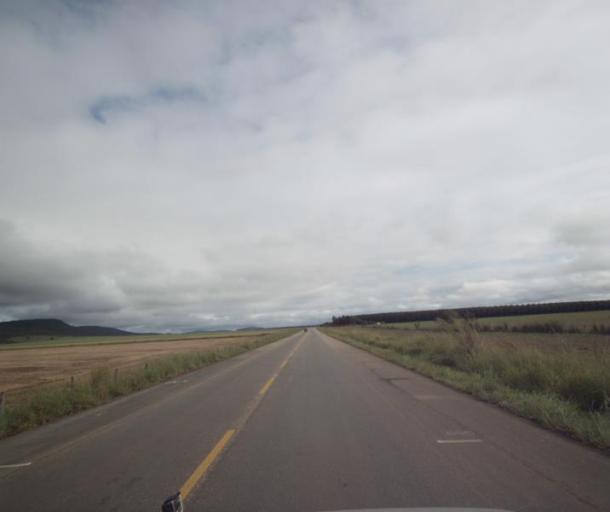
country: BR
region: Goias
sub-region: Padre Bernardo
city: Padre Bernardo
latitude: -15.3836
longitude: -48.6423
